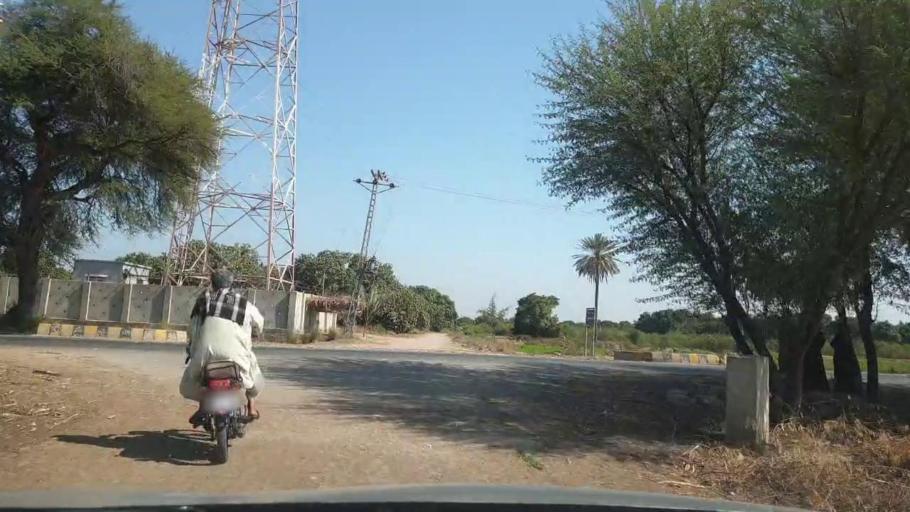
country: PK
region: Sindh
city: Tando Adam
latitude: 25.6357
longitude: 68.6842
